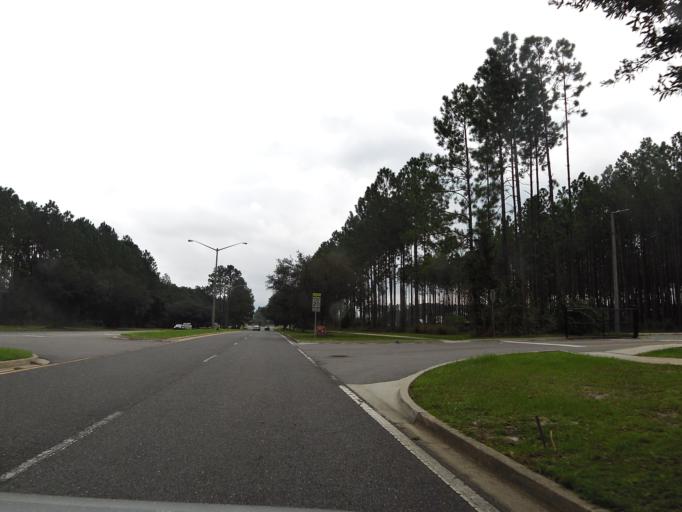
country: US
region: Florida
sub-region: Clay County
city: Lakeside
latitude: 30.1652
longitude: -81.8456
